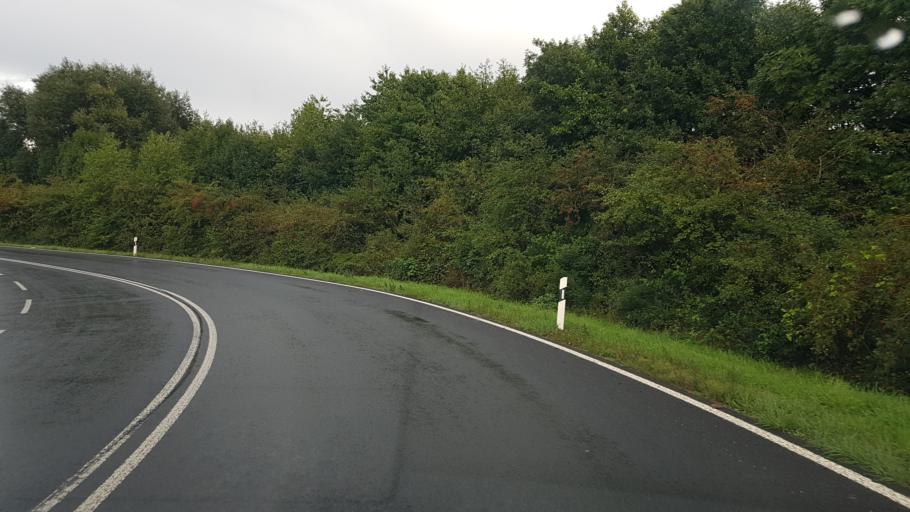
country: DE
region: Thuringia
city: Saalfeld
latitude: 50.6574
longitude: 11.3806
